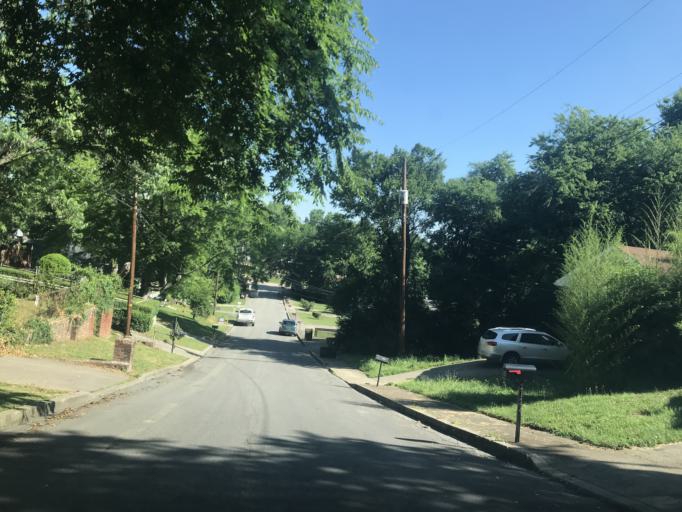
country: US
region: Tennessee
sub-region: Davidson County
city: Nashville
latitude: 36.1868
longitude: -86.8084
